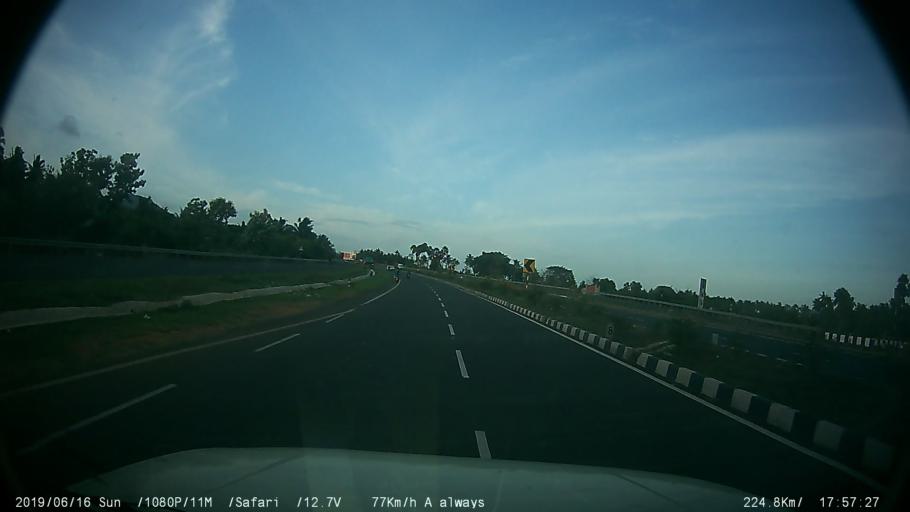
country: IN
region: Tamil Nadu
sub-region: Coimbatore
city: Madukkarai
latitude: 10.8728
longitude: 76.9026
